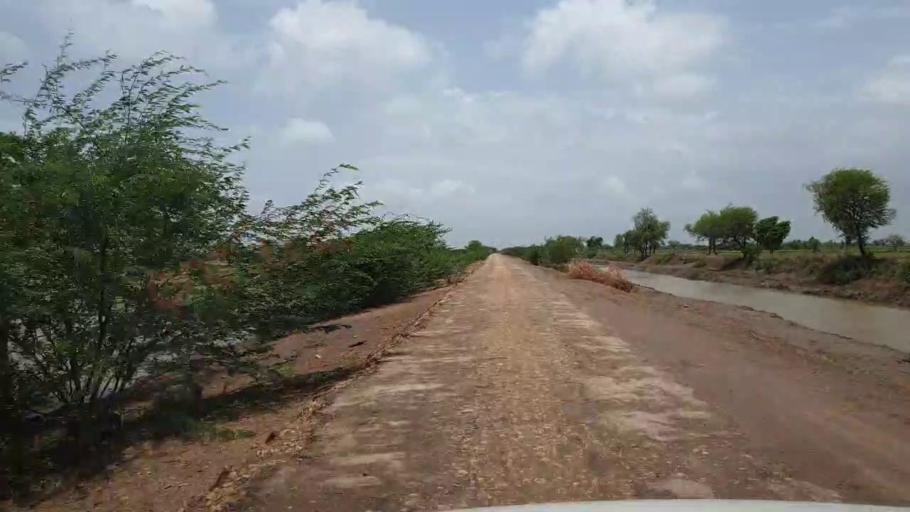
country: PK
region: Sindh
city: Kario
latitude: 24.7102
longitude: 68.5996
